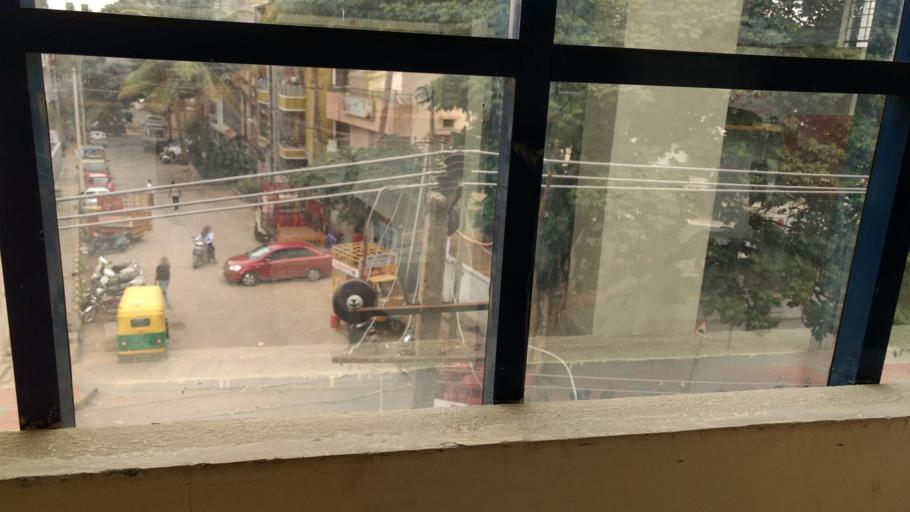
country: IN
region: Karnataka
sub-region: Bangalore Urban
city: Bangalore
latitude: 13.0221
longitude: 77.6391
